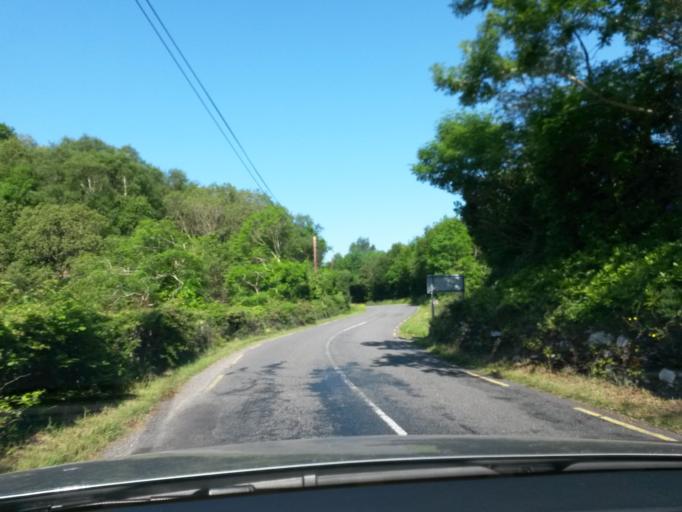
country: IE
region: Munster
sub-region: Ciarrai
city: Kenmare
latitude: 51.7622
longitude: -9.7862
